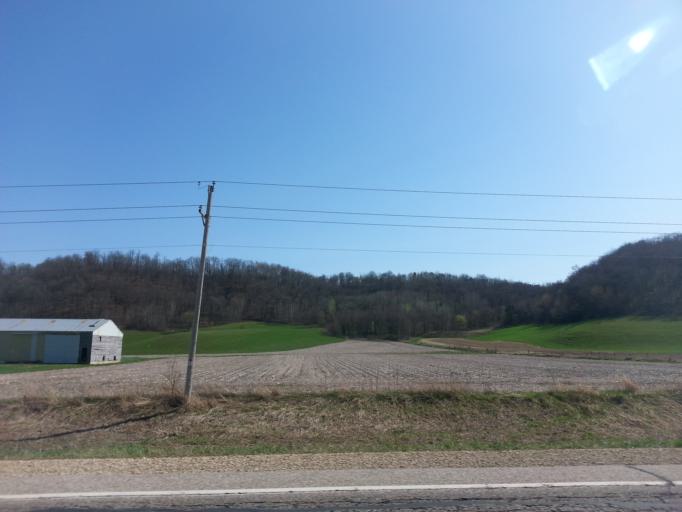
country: US
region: Wisconsin
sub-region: Pepin County
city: Durand
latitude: 44.6403
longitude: -92.0887
